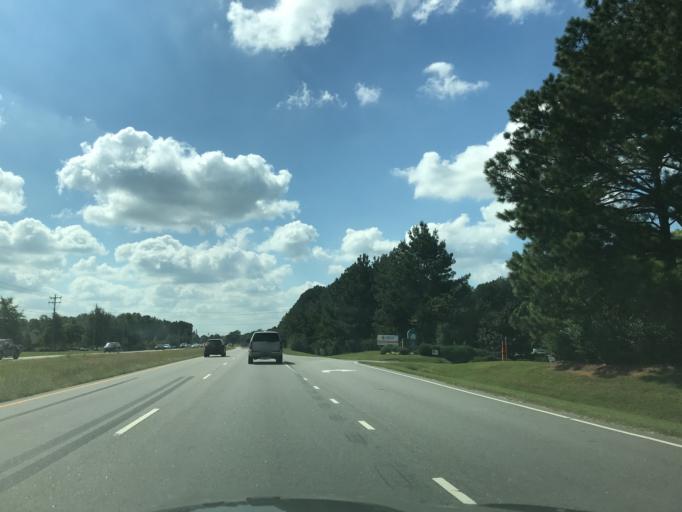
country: US
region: North Carolina
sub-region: Wake County
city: Wake Forest
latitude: 35.9887
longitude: -78.5326
